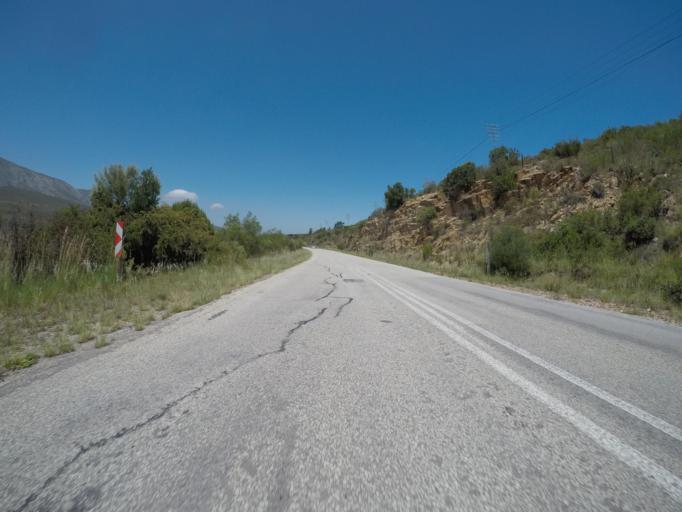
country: ZA
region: Eastern Cape
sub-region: Cacadu District Municipality
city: Kareedouw
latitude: -33.9122
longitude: 24.1689
